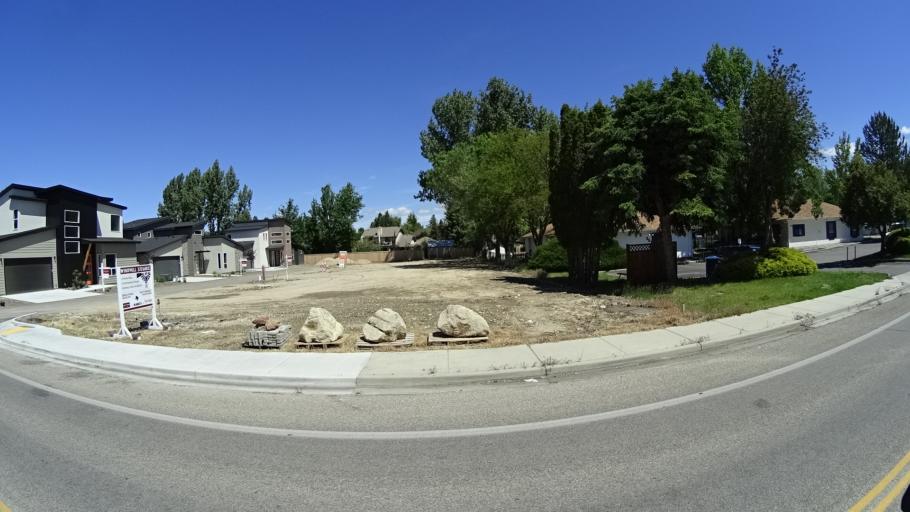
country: US
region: Idaho
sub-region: Ada County
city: Boise
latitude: 43.5861
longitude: -116.1796
